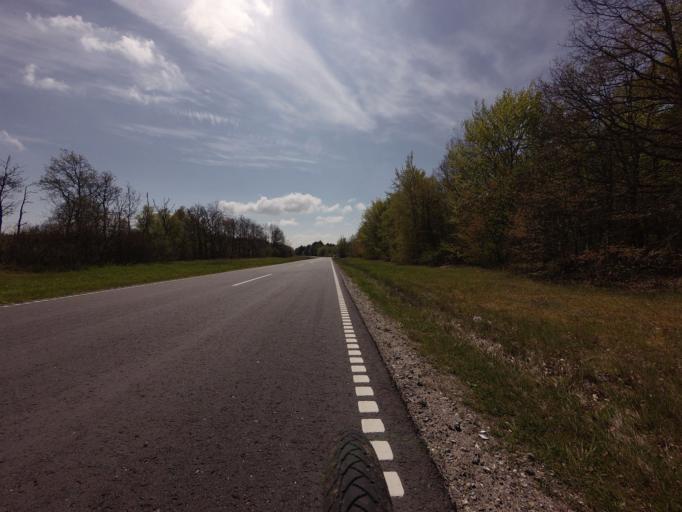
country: DK
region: North Denmark
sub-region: Jammerbugt Kommune
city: Brovst
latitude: 57.1646
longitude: 9.5756
